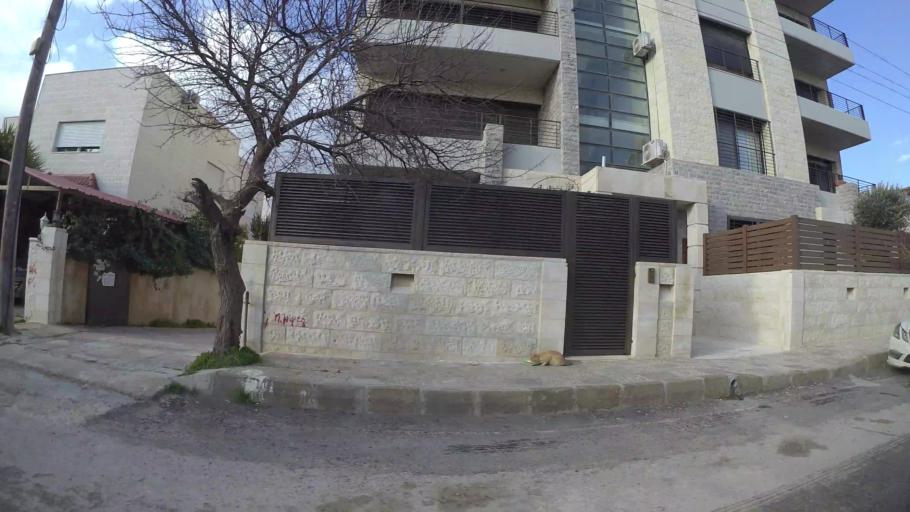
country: JO
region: Amman
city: Al Bunayyat ash Shamaliyah
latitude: 31.9085
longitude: 35.8730
